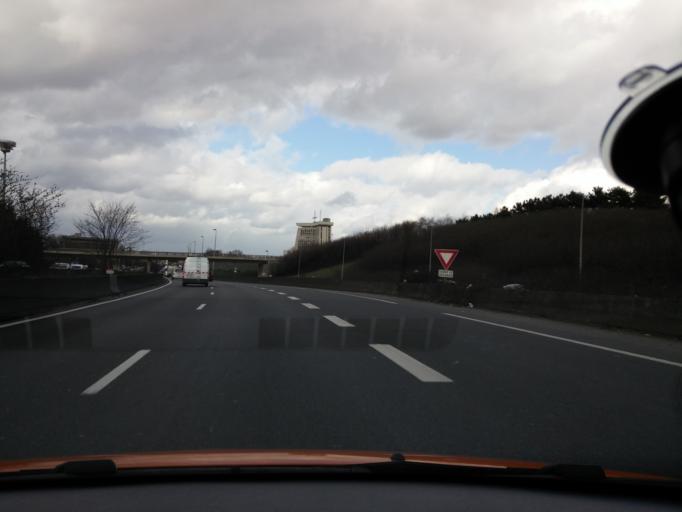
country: FR
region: Ile-de-France
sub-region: Departement du Val-de-Marne
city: Creteil
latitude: 48.7800
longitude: 2.4415
